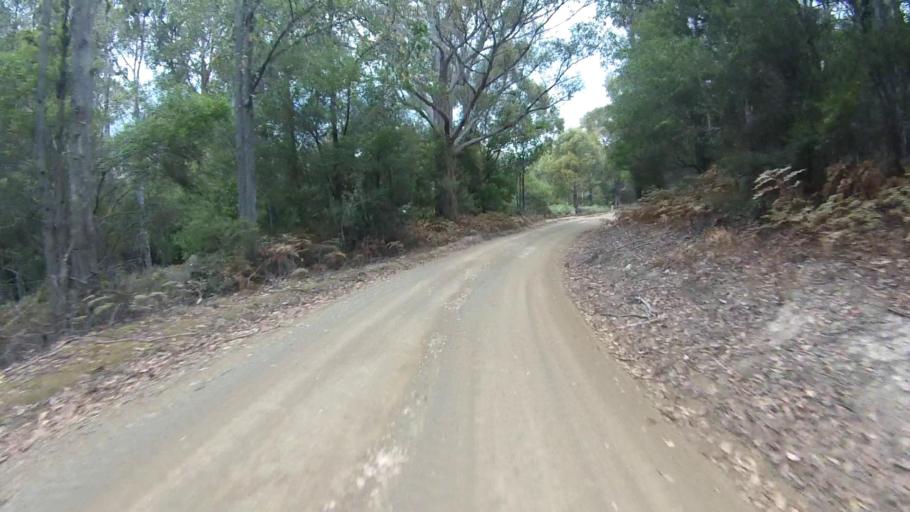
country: AU
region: Tasmania
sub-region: Huon Valley
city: Huonville
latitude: -42.9595
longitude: 147.0513
